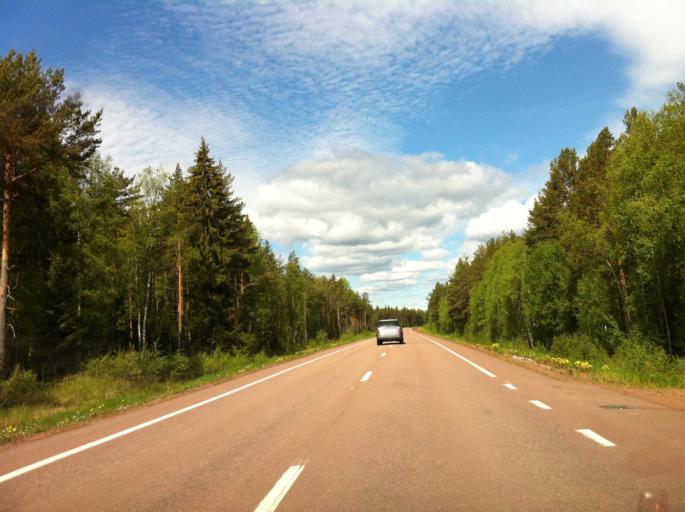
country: SE
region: Dalarna
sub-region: Mora Kommun
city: Mora
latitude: 60.9232
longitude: 14.5794
